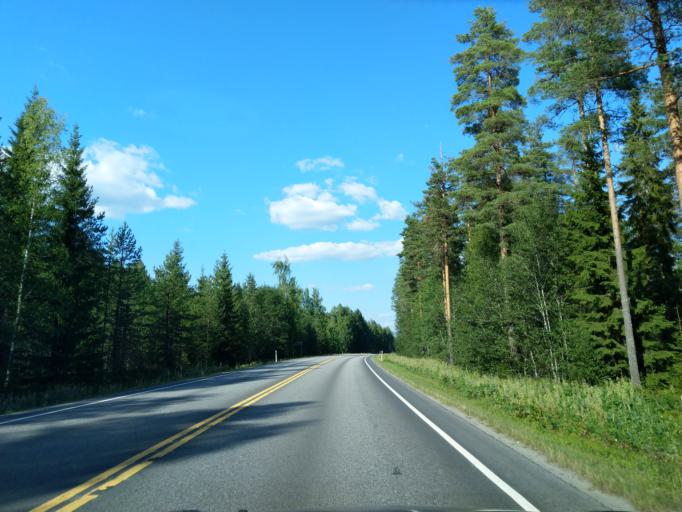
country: FI
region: Pirkanmaa
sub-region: Luoteis-Pirkanmaa
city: Kihnioe
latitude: 62.1250
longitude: 23.1126
